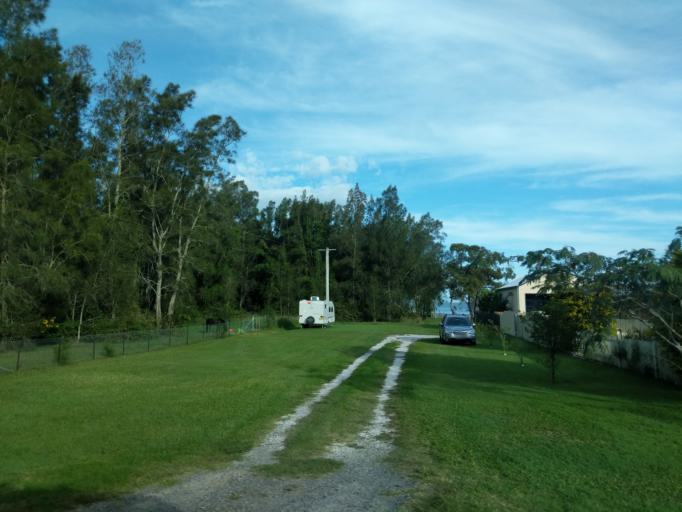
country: AU
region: New South Wales
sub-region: Port Stephens Shire
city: Port Stephens
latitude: -32.6663
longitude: 152.0151
